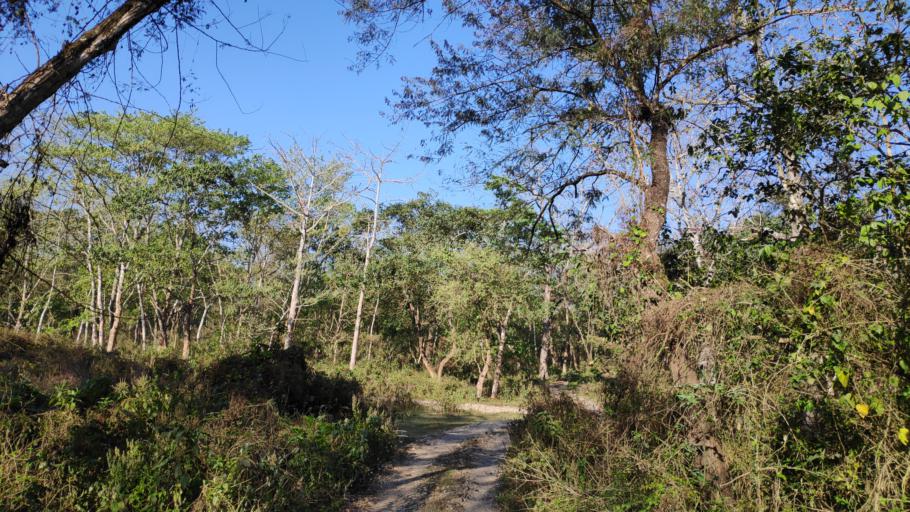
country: NP
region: Central Region
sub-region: Narayani Zone
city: Bharatpur
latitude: 27.5593
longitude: 84.5431
